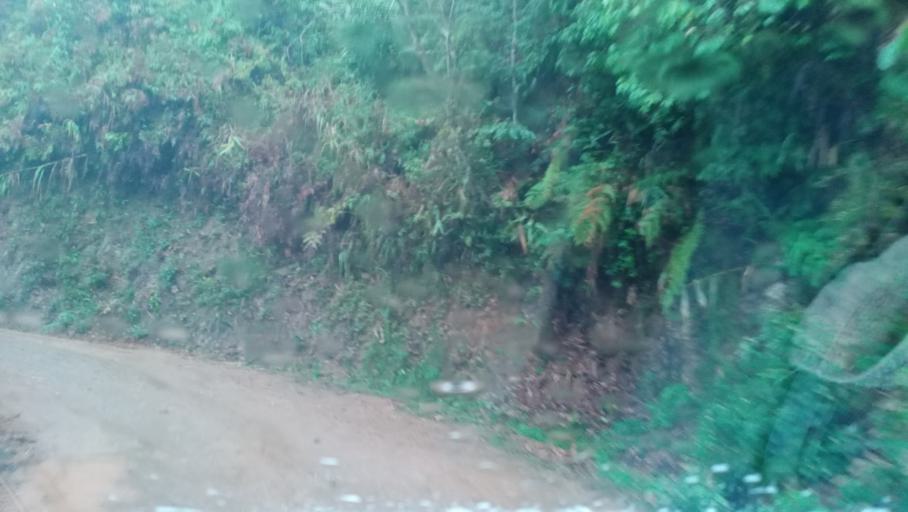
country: LA
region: Phongsali
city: Khoa
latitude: 21.1957
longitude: 102.2918
